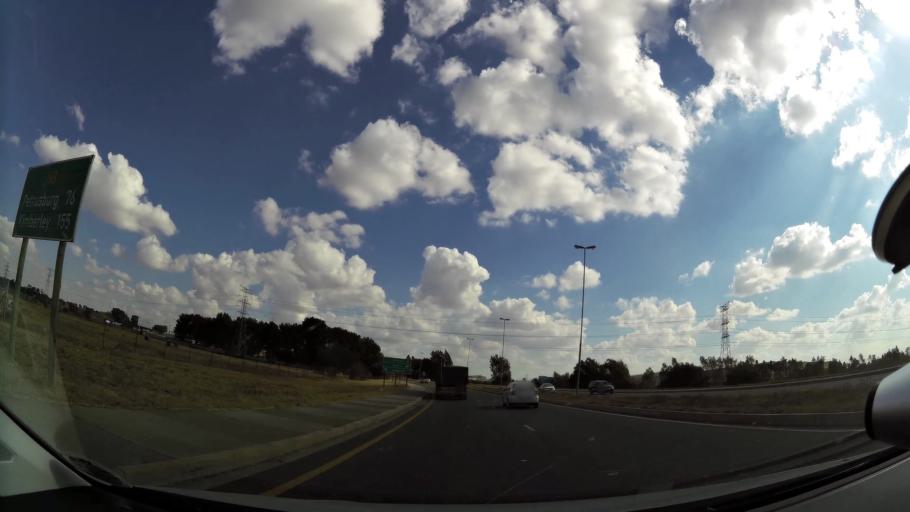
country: ZA
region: Orange Free State
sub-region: Mangaung Metropolitan Municipality
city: Bloemfontein
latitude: -29.1272
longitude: 26.1598
